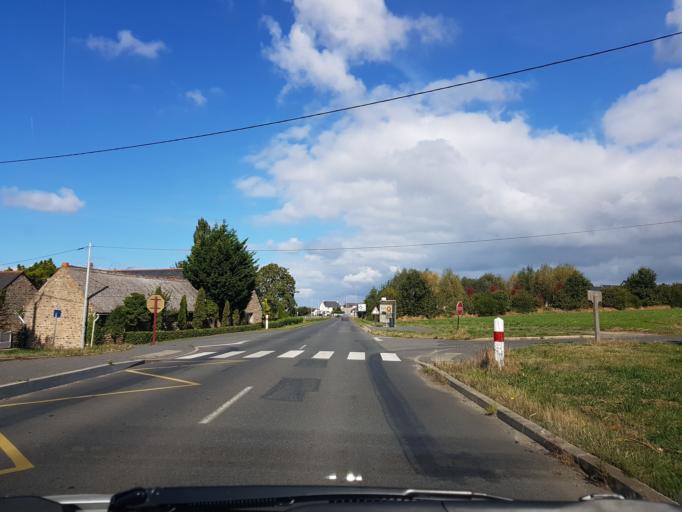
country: FR
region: Brittany
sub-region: Departement des Cotes-d'Armor
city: Langueux
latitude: 48.4807
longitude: -2.7492
